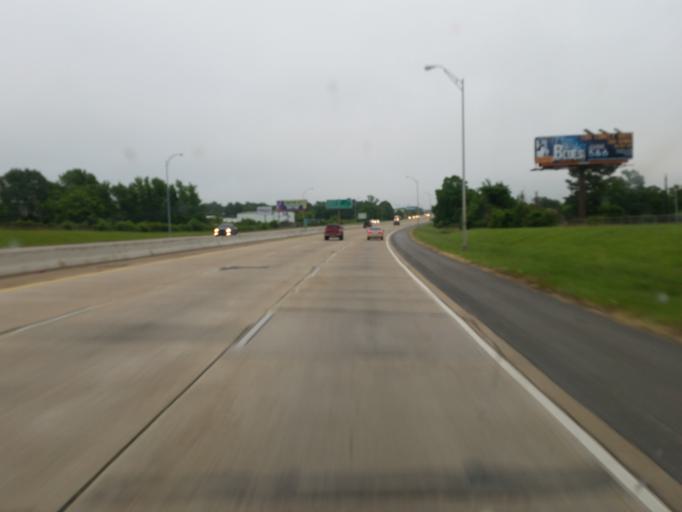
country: US
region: Louisiana
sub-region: Caddo Parish
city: Shreveport
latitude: 32.4666
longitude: -93.8142
